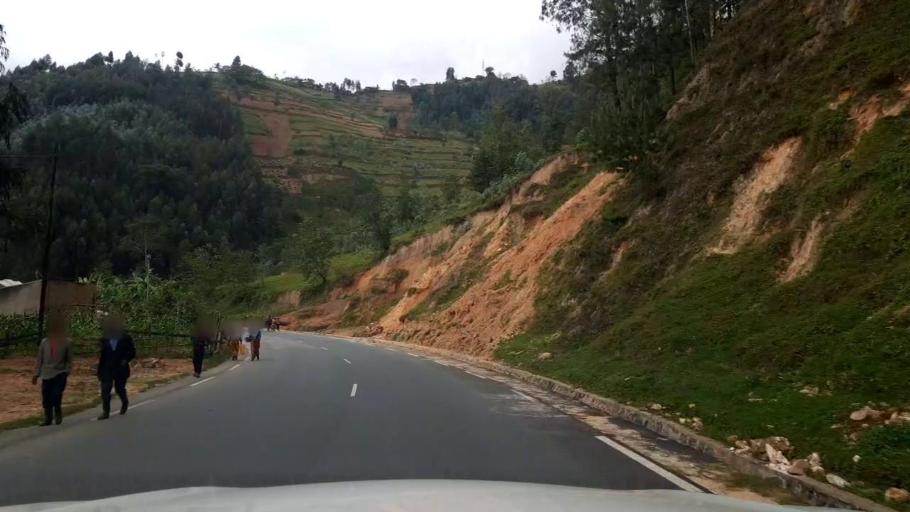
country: RW
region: Northern Province
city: Musanze
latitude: -1.6932
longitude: 29.5568
